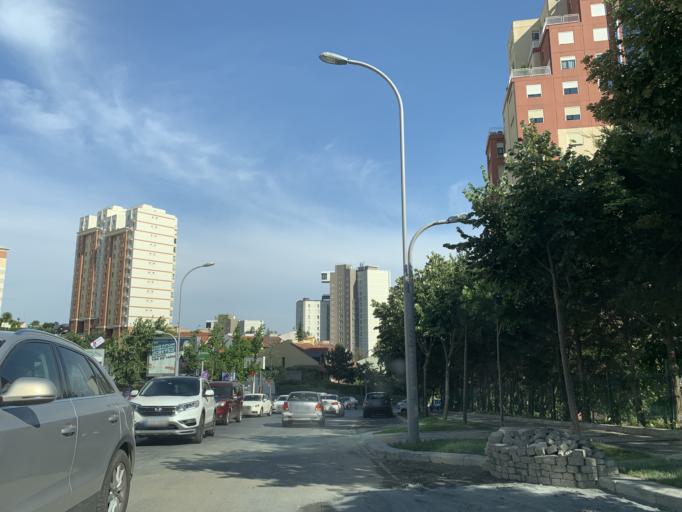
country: TR
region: Istanbul
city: Esenyurt
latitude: 41.0724
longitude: 28.6837
